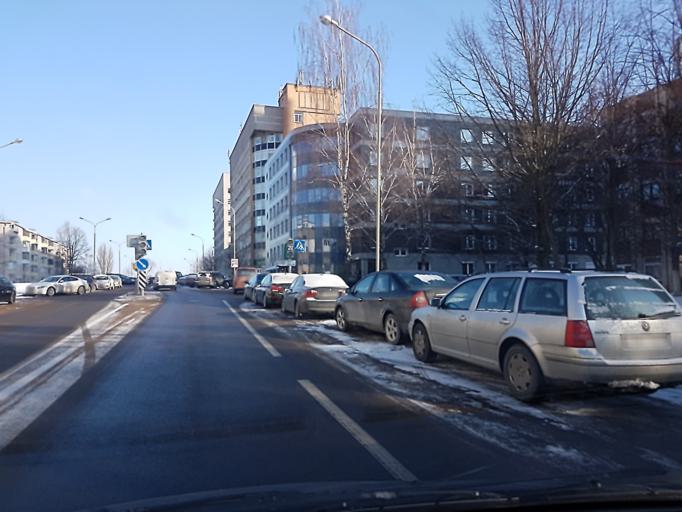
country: BY
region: Minsk
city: Minsk
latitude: 53.9101
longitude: 27.5160
